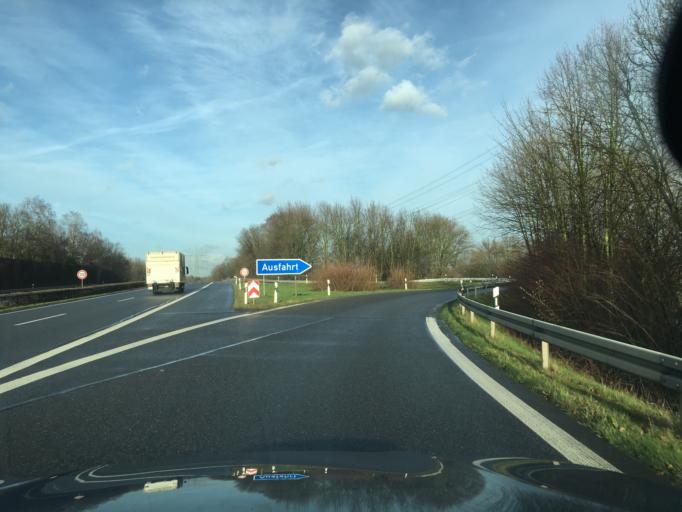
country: DE
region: North Rhine-Westphalia
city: Bruhl
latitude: 50.8279
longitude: 6.9326
